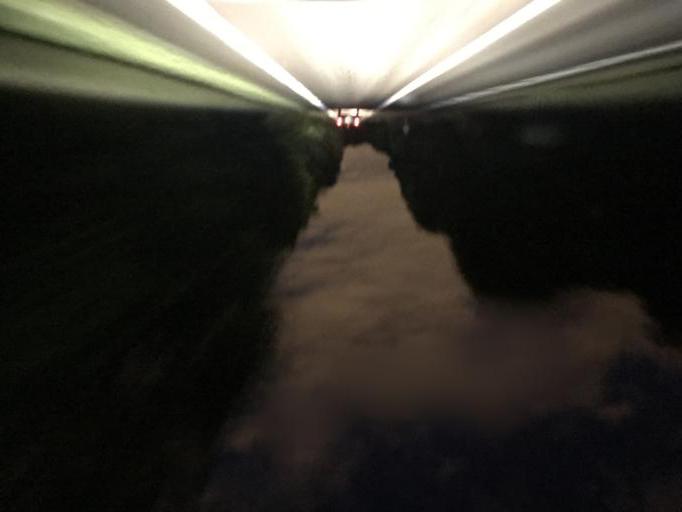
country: FR
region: Ile-de-France
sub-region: Departement des Yvelines
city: Le Mesnil-le-Roi
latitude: 48.9417
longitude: 2.1110
